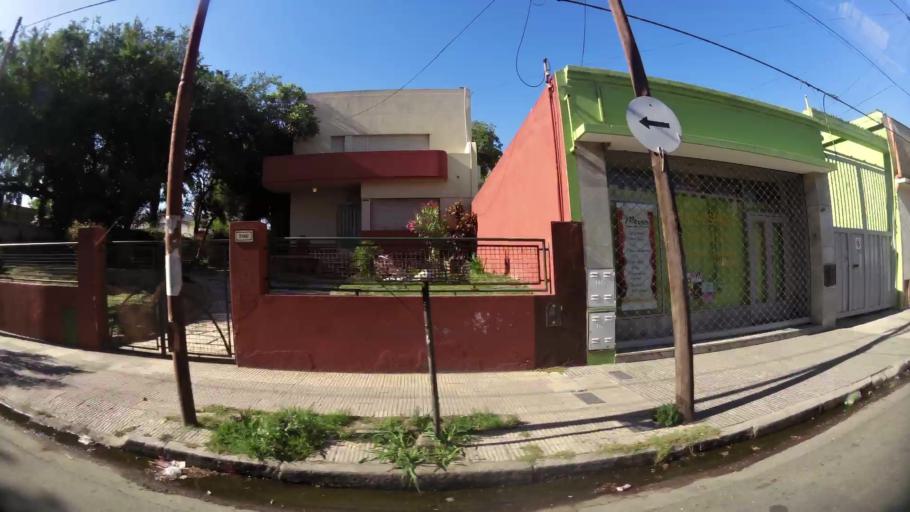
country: AR
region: Cordoba
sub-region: Departamento de Capital
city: Cordoba
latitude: -31.4252
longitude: -64.1526
